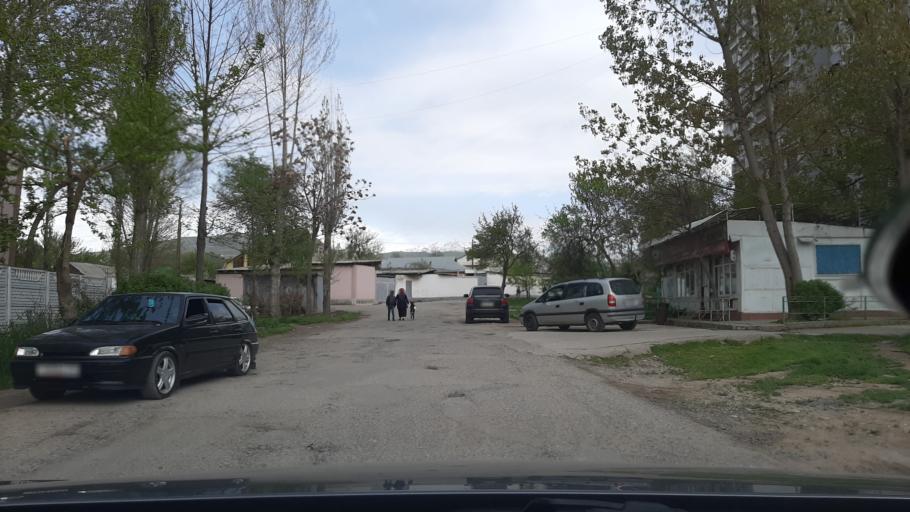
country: TJ
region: Dushanbe
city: Dushanbe
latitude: 38.5886
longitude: 68.7490
